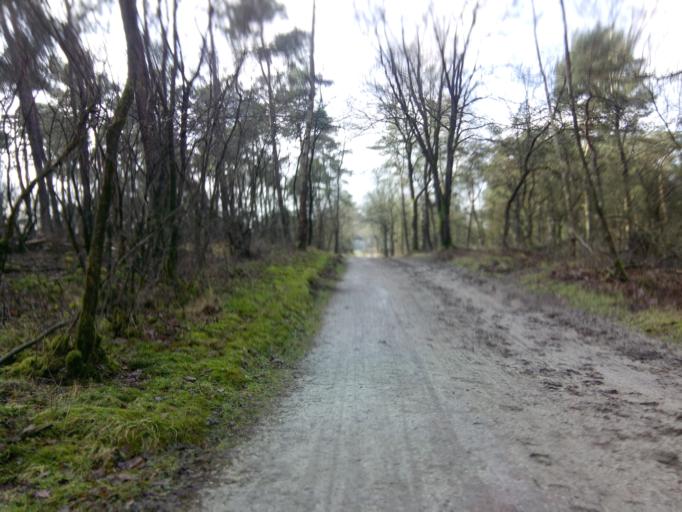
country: NL
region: Utrecht
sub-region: Gemeente Utrechtse Heuvelrug
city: Leersum
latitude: 52.0372
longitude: 5.4427
